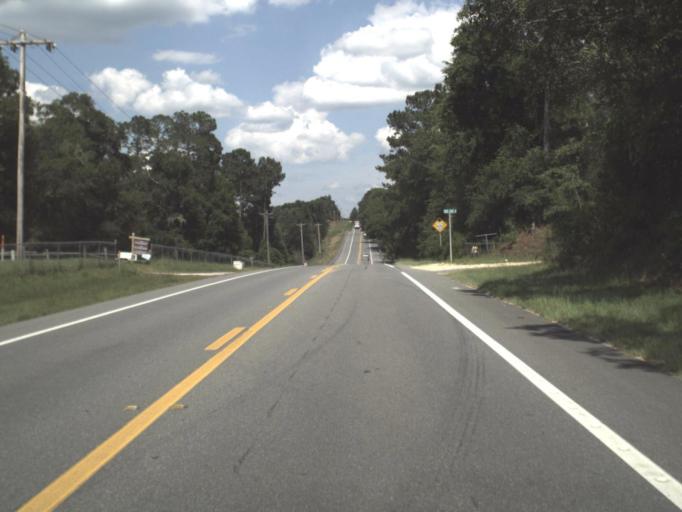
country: US
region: Florida
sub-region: Putnam County
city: Interlachen
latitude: 29.7270
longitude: -81.9291
